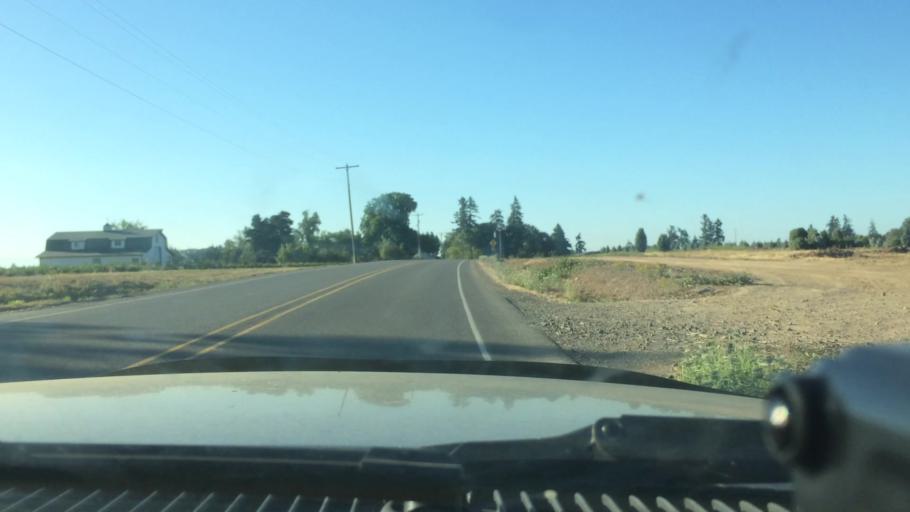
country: US
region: Oregon
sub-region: Marion County
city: Gervais
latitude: 45.1224
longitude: -122.9861
